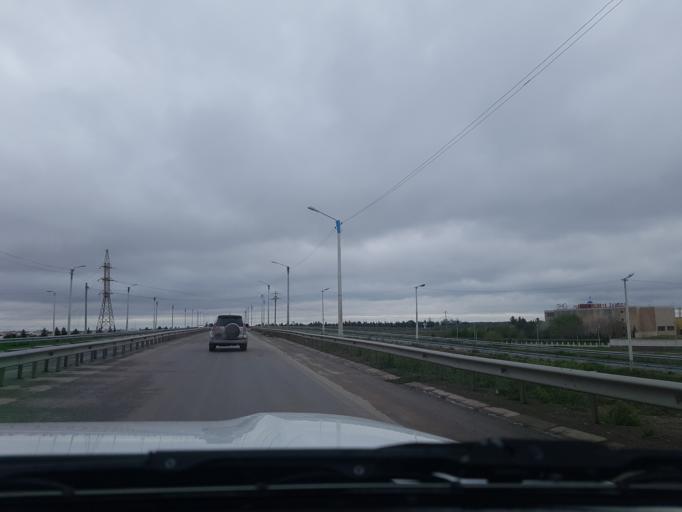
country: TM
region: Mary
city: Mary
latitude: 37.5941
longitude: 61.8856
